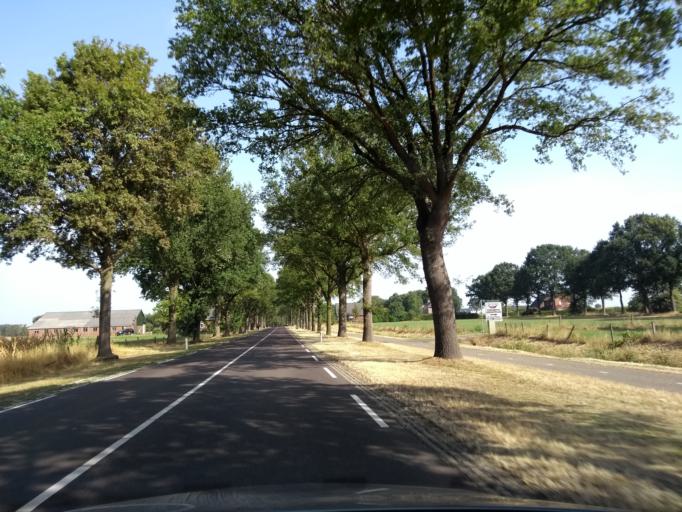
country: NL
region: Overijssel
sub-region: Gemeente Twenterand
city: Vroomshoop
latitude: 52.4243
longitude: 6.5473
